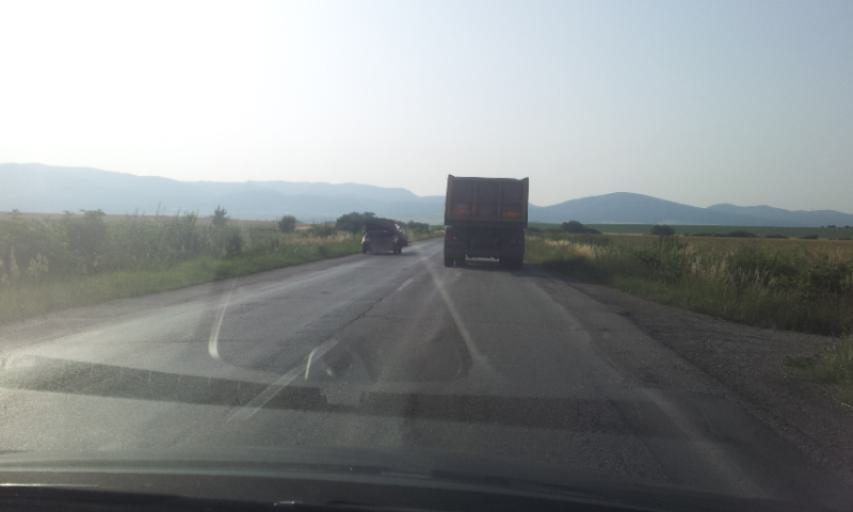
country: SK
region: Kosicky
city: Kosice
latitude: 48.6114
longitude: 21.2842
